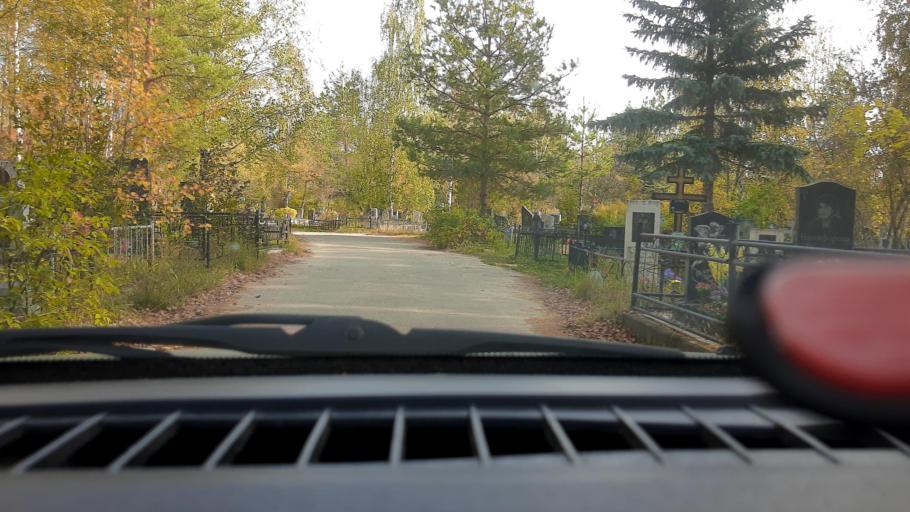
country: RU
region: Nizjnij Novgorod
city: Gorbatovka
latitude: 56.3547
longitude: 43.7821
